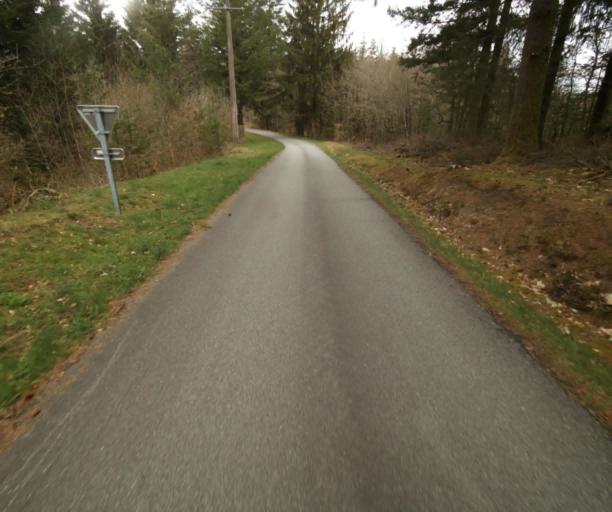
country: FR
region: Limousin
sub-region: Departement de la Correze
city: Correze
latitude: 45.3332
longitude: 1.9523
